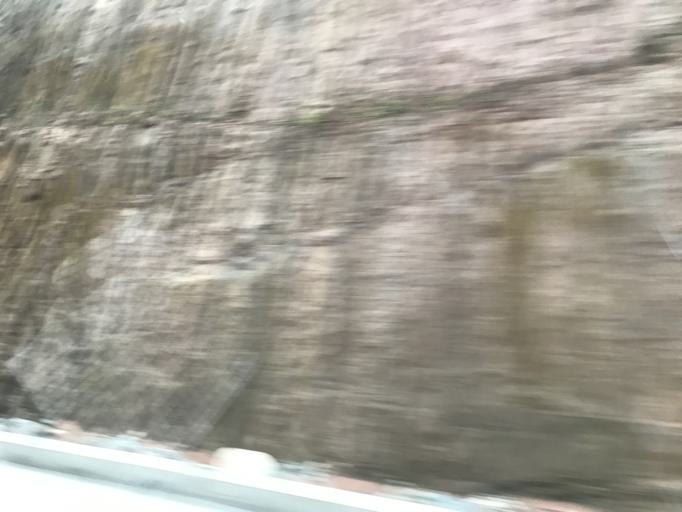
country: EC
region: Napo
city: Tena
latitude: -1.0622
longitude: -77.7022
